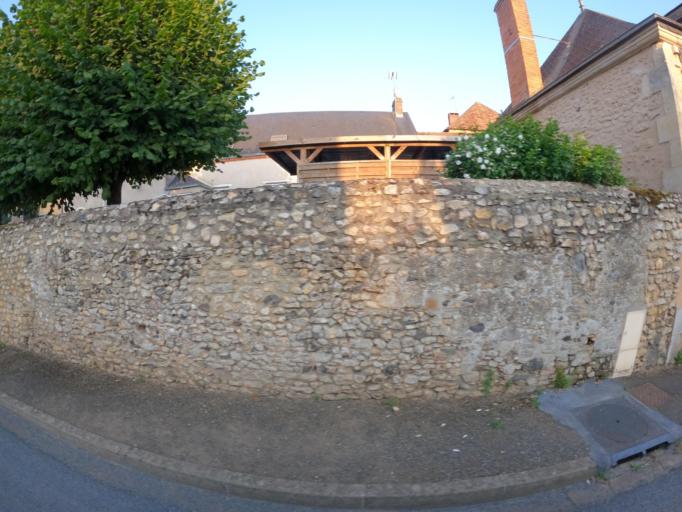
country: FR
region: Pays de la Loire
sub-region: Departement de la Sarthe
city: Parce-sur-Sarthe
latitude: 47.9037
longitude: -0.2215
